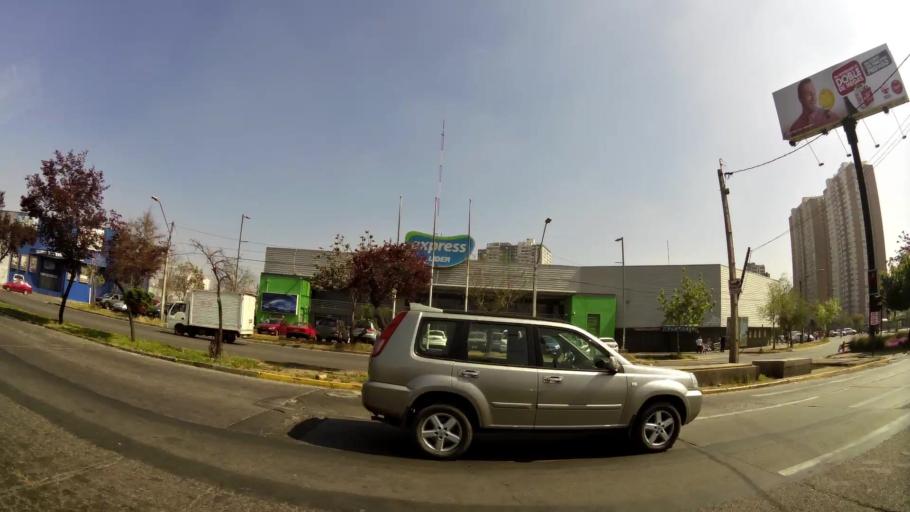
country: CL
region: Santiago Metropolitan
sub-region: Provincia de Santiago
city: Santiago
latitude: -33.4556
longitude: -70.6264
